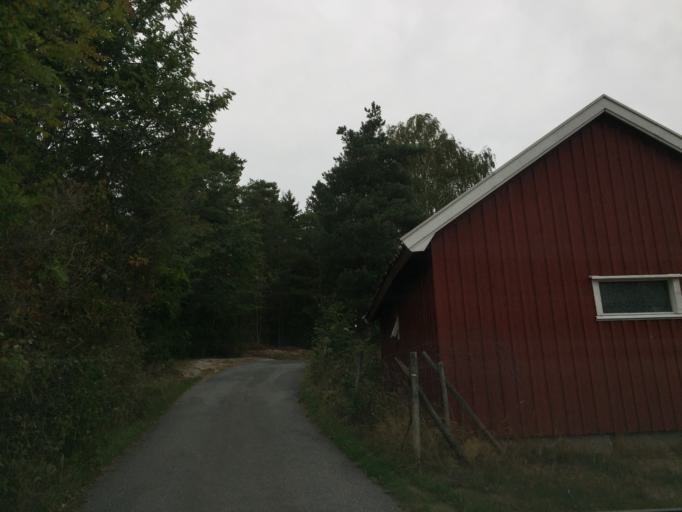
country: NO
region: Ostfold
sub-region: Hvaler
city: Skjaerhalden
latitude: 59.0771
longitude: 11.0055
